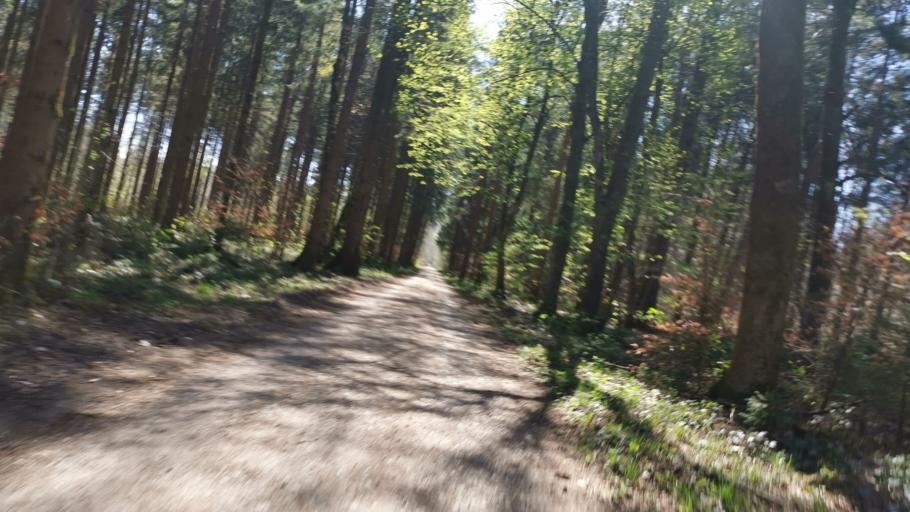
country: DE
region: Bavaria
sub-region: Upper Bavaria
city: Planegg
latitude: 48.0885
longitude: 11.4330
